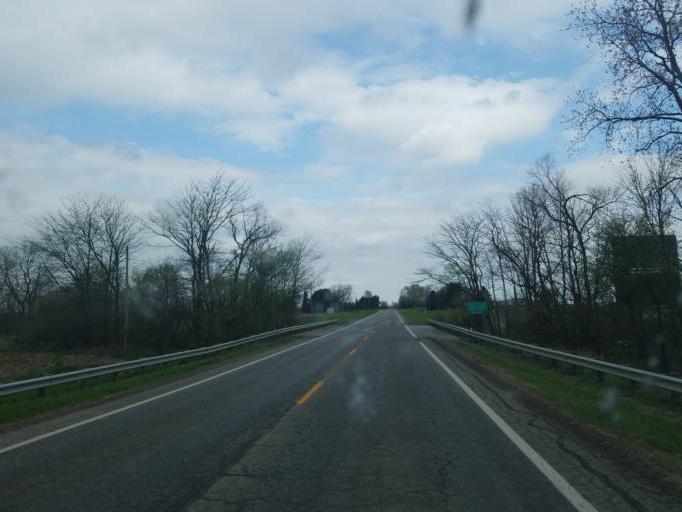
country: US
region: Ohio
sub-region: Morrow County
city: Mount Gilead
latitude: 40.5776
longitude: -82.8967
